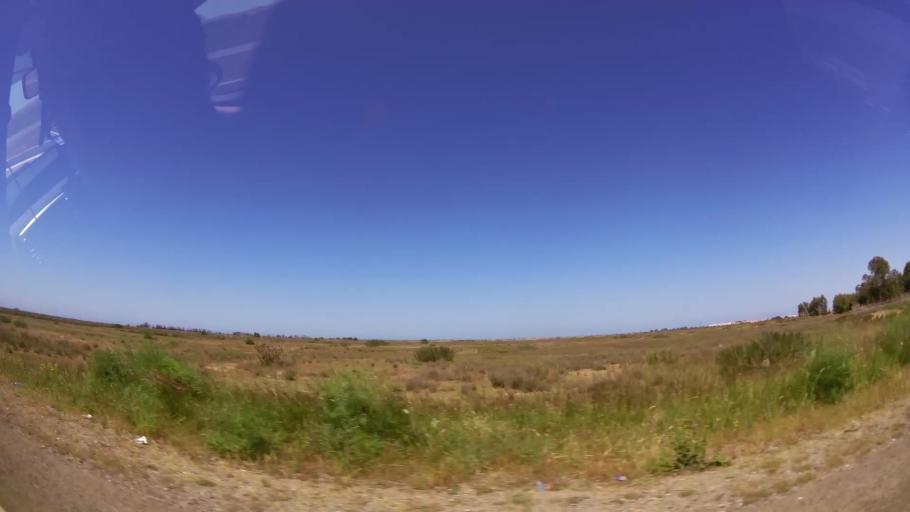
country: MA
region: Oriental
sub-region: Berkane-Taourirt
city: Madagh
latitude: 35.1034
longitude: -2.3405
